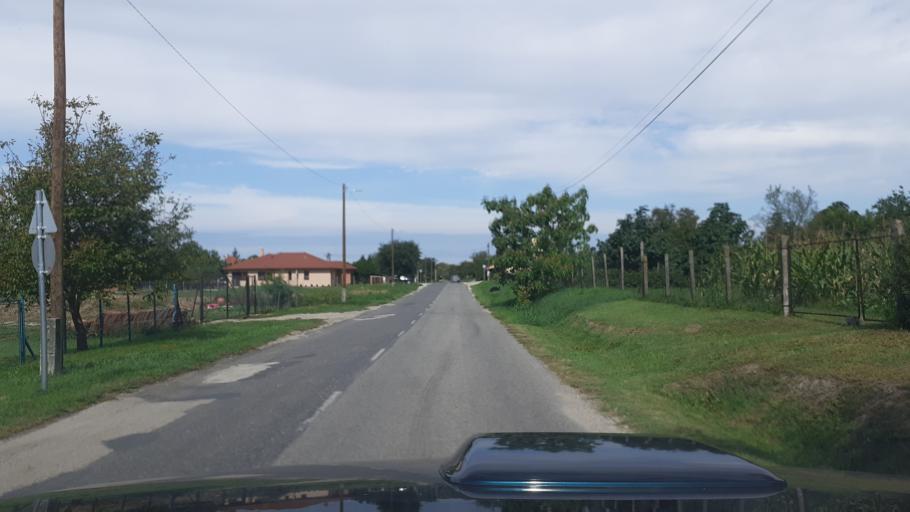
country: HU
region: Fejer
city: Seregelyes
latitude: 47.1156
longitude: 18.5864
